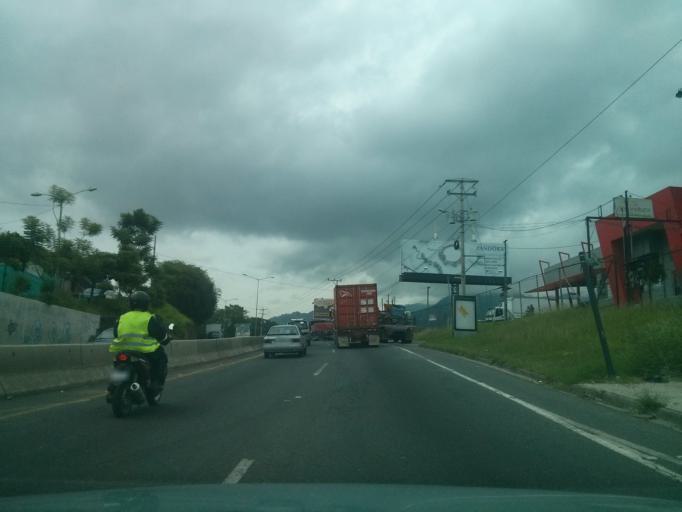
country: CR
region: San Jose
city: San Rafael
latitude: 9.9299
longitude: -84.1164
